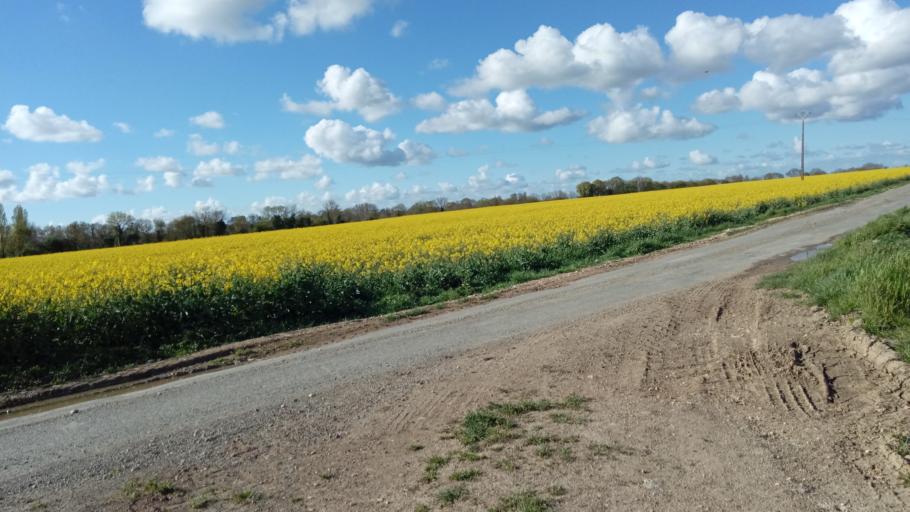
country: FR
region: Poitou-Charentes
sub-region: Departement de la Charente-Maritime
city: Verines
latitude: 46.1670
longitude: -0.9412
